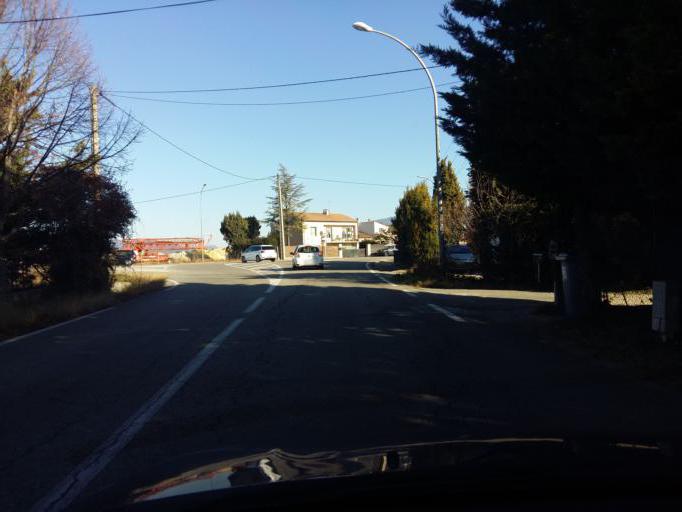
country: FR
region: Provence-Alpes-Cote d'Azur
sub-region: Departement du Vaucluse
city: Valreas
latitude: 44.3864
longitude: 4.9761
